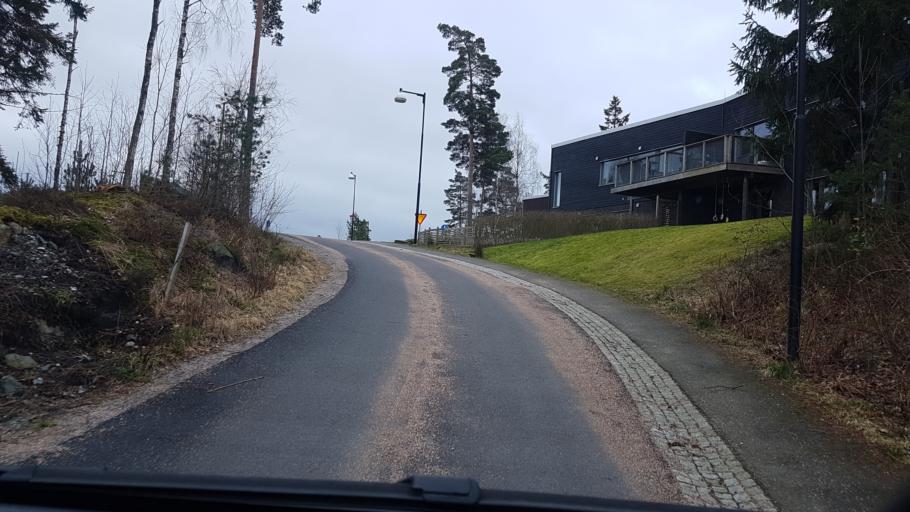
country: SE
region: Vaestra Goetaland
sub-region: Lerums Kommun
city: Lerum
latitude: 57.7855
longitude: 12.2740
